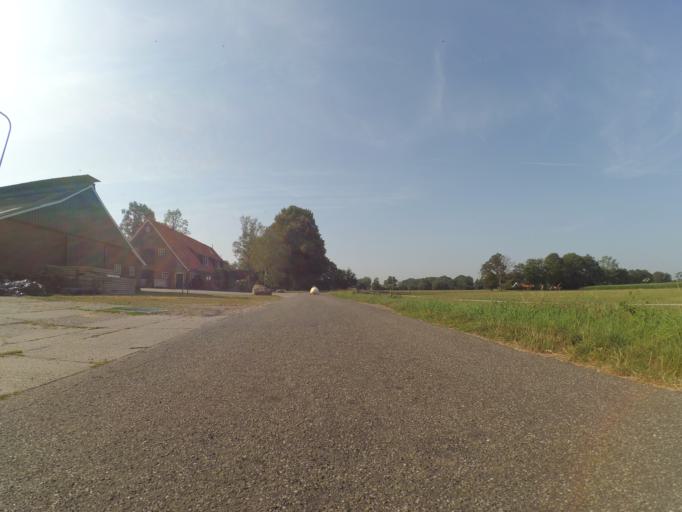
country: NL
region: Overijssel
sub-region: Gemeente Oldenzaal
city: Oldenzaal
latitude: 52.3673
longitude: 6.8634
